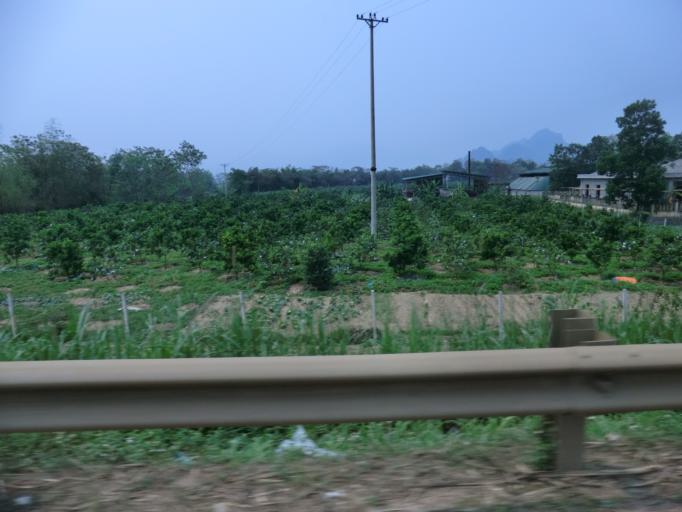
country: VN
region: Thanh Hoa
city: Thi Tran Thuong Xuan
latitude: 19.9184
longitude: 105.3948
